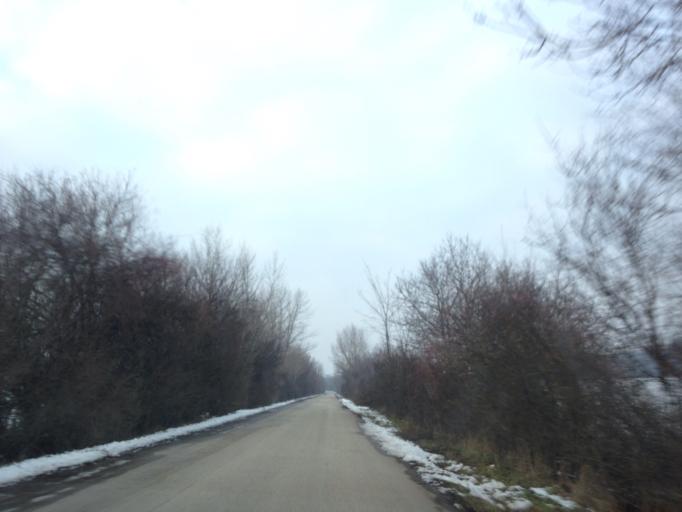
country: SK
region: Nitriansky
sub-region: Okres Nitra
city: Vrable
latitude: 48.0887
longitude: 18.3693
